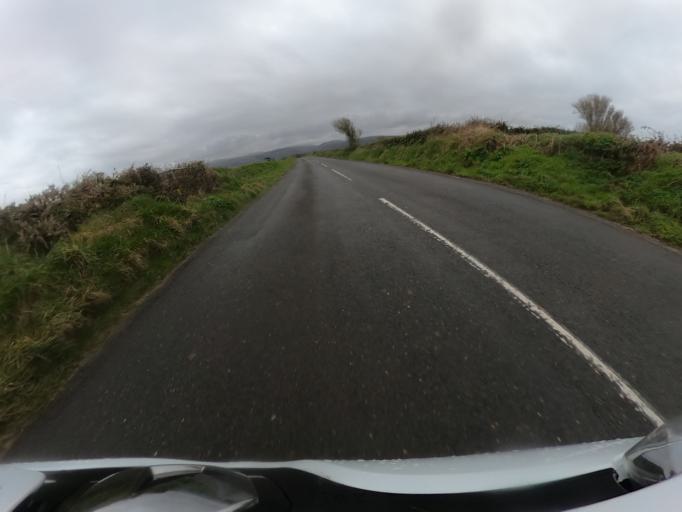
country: IM
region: Ramsey
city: Ramsey
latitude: 54.3537
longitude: -4.5073
